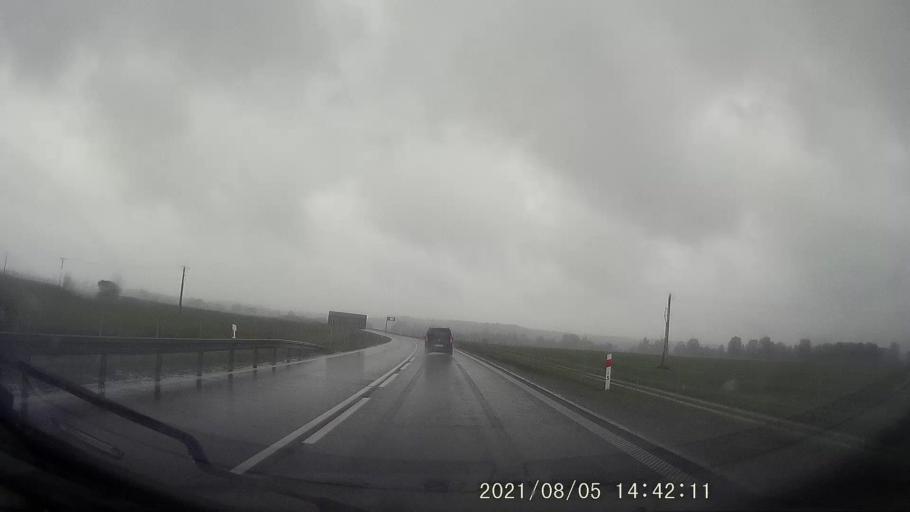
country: PL
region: Opole Voivodeship
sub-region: Powiat nyski
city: Nysa
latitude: 50.4722
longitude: 17.4060
